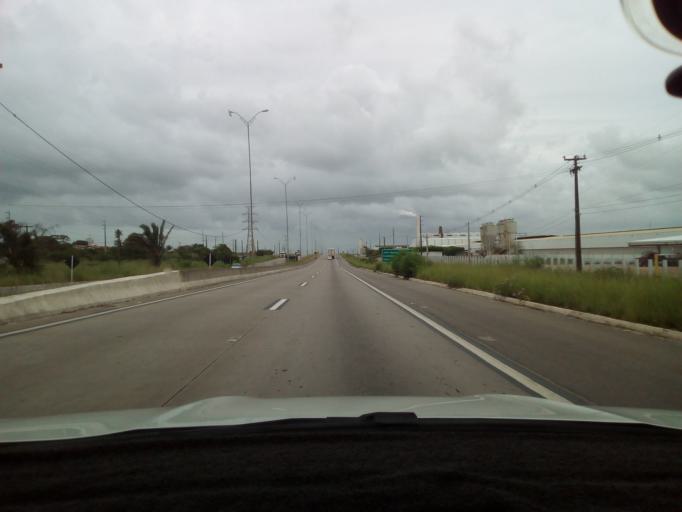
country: BR
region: Paraiba
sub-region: Conde
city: Conde
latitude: -7.2559
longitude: -34.9346
